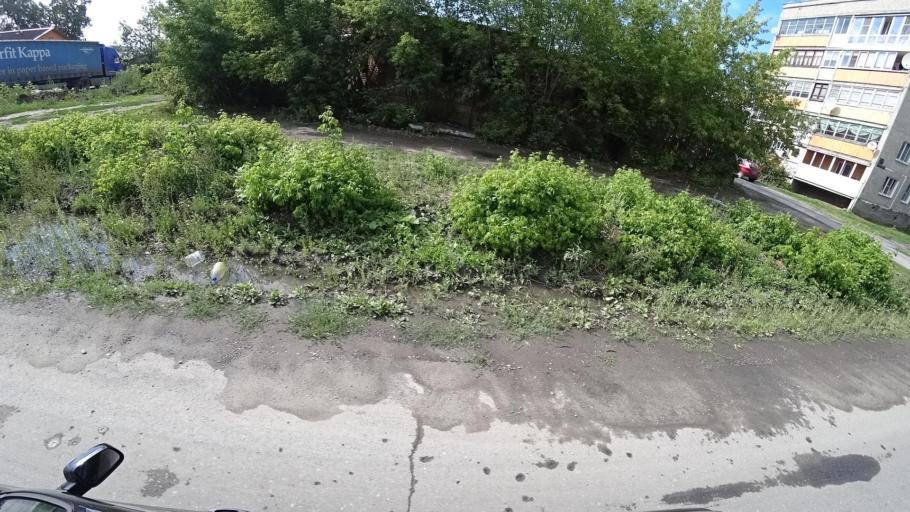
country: RU
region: Sverdlovsk
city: Kamyshlov
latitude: 56.8404
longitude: 62.7126
